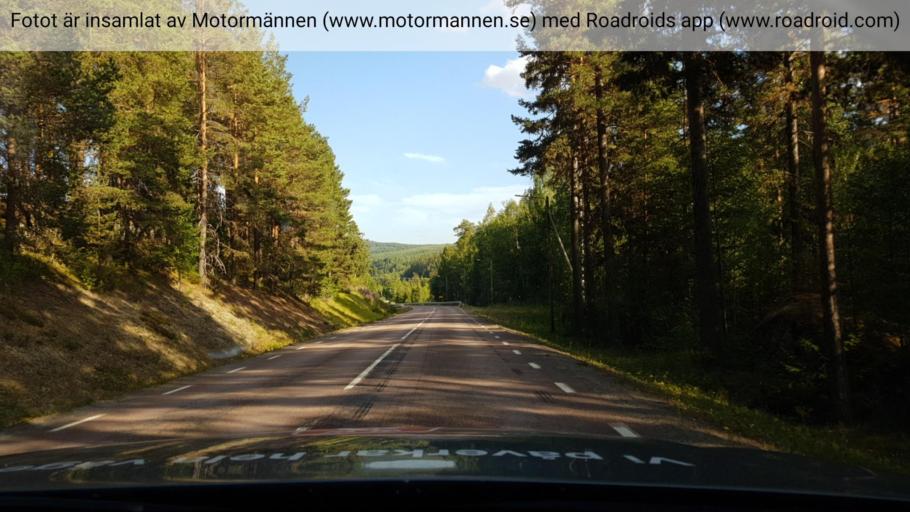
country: SE
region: Vaesternorrland
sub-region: Solleftea Kommun
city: As
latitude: 63.5841
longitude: 16.3363
